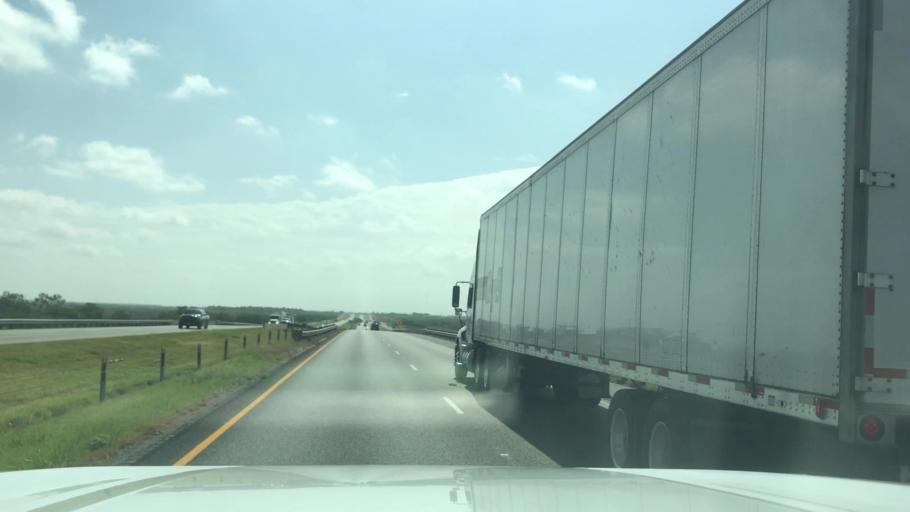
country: US
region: Texas
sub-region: Taylor County
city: Merkel
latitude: 32.4630
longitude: -99.9548
